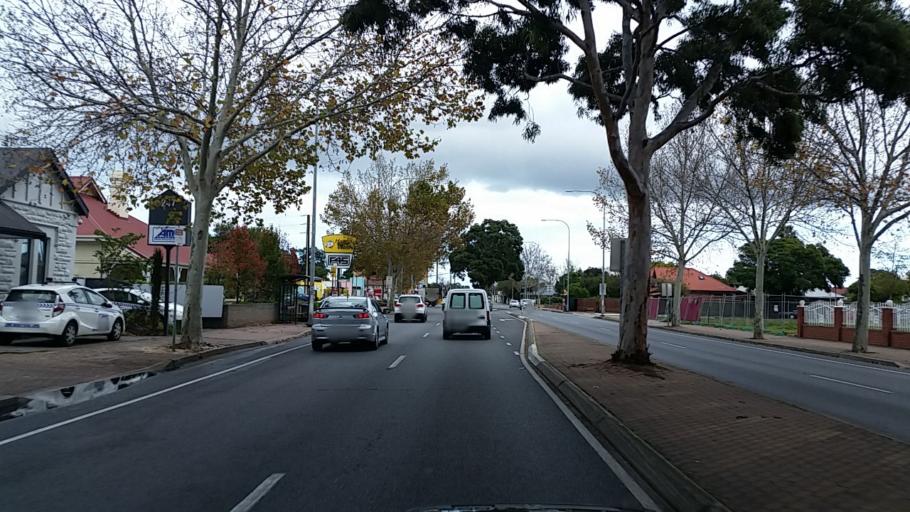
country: AU
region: South Australia
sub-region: City of West Torrens
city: Thebarton
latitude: -34.9245
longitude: 138.5538
